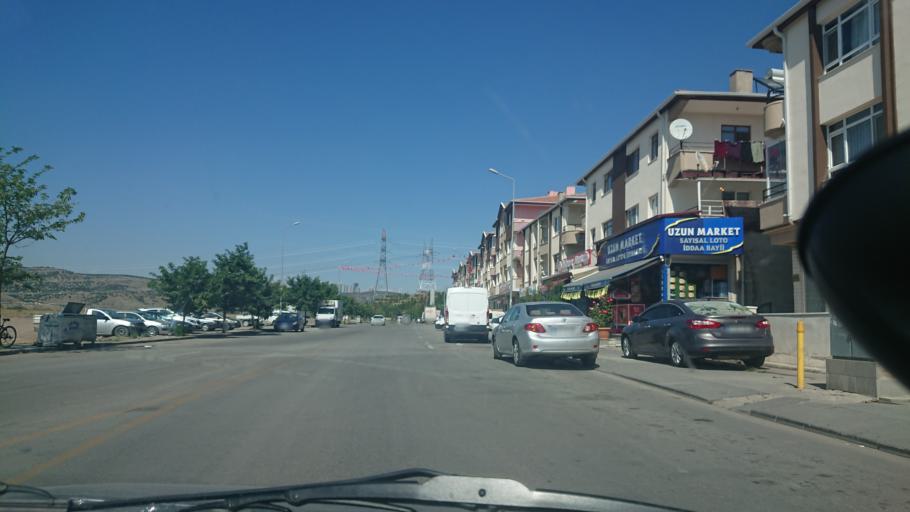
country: TR
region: Ankara
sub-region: Goelbasi
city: Golbasi
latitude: 39.8004
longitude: 32.8126
